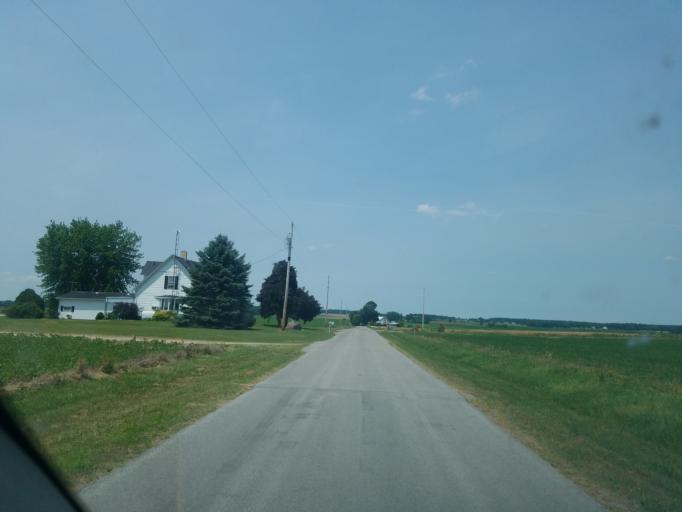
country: US
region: Ohio
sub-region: Wyandot County
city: Carey
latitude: 41.0106
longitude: -83.4489
